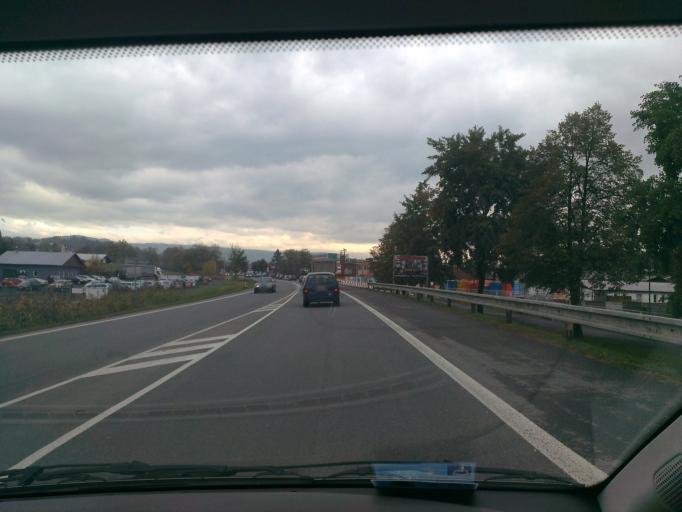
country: CZ
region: Zlin
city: Valasske Mezirici
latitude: 49.4888
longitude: 17.9615
